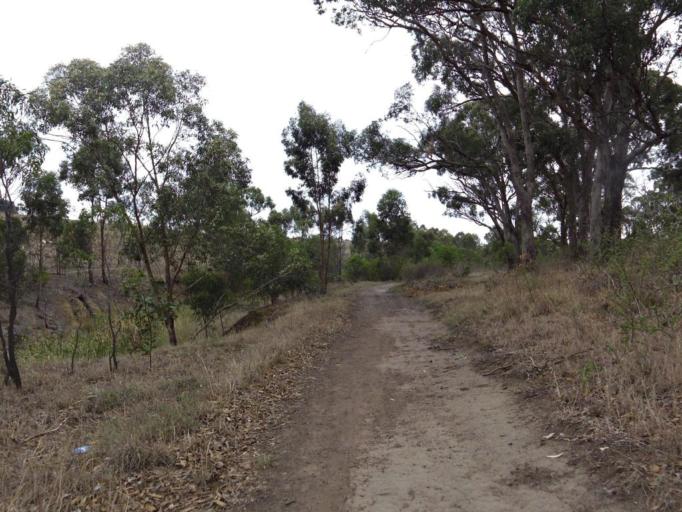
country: AU
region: Victoria
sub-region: Hume
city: Attwood
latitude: -37.6675
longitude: 144.8998
